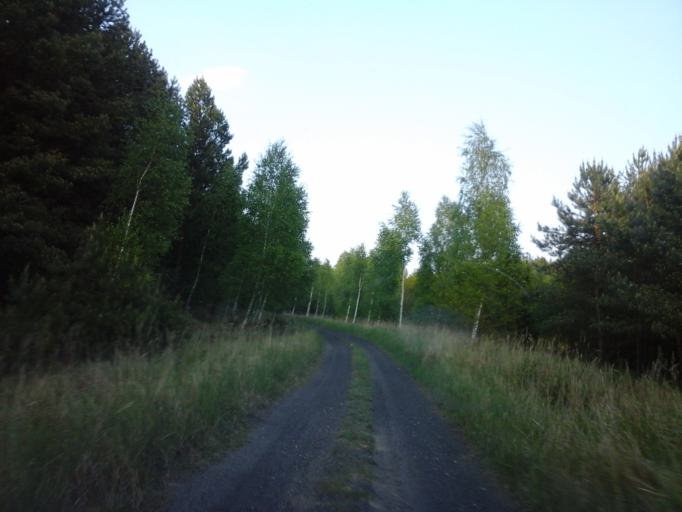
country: PL
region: West Pomeranian Voivodeship
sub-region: Powiat choszczenski
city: Krzecin
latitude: 53.0055
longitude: 15.5321
